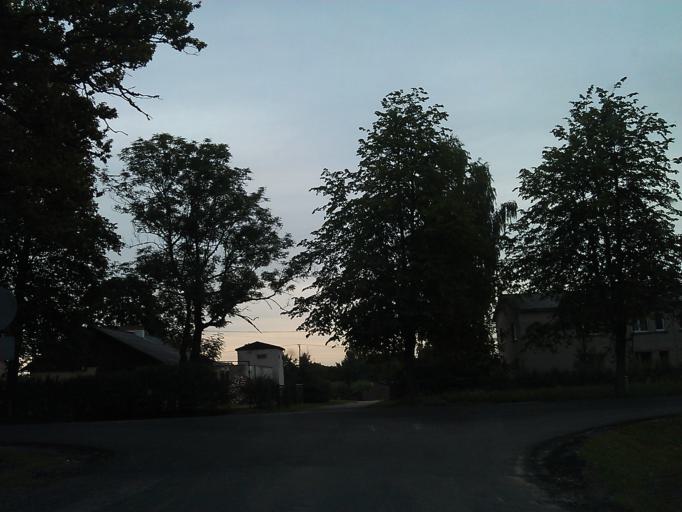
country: LV
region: Amatas Novads
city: Drabesi
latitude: 57.2068
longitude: 25.1646
